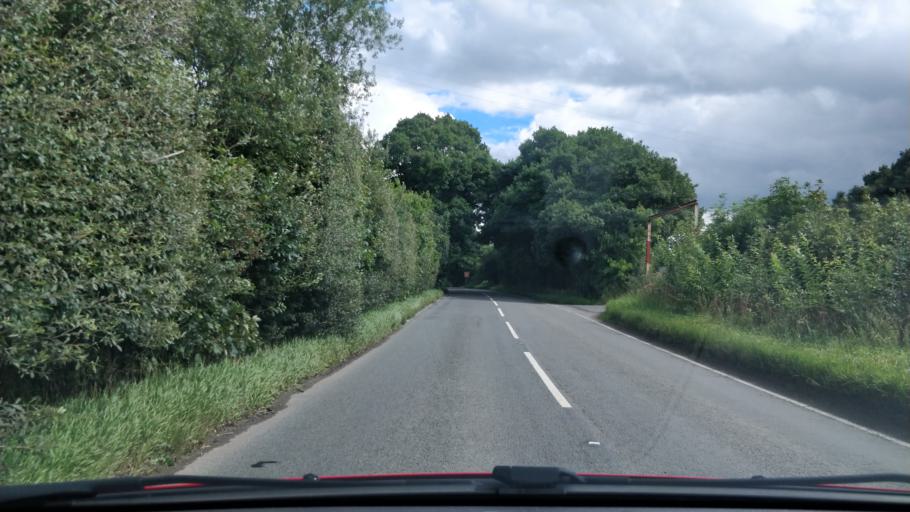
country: GB
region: Wales
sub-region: County of Flintshire
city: Hope
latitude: 53.1124
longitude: -3.0236
